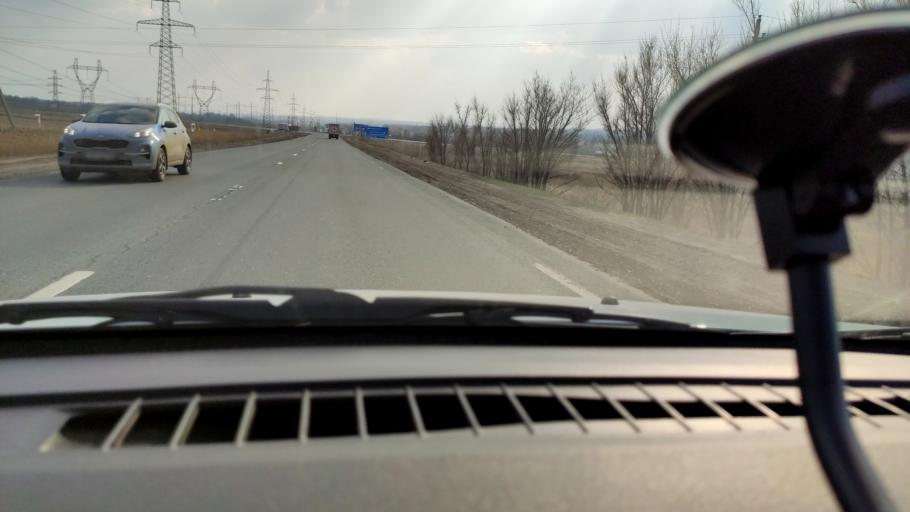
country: RU
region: Samara
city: Dubovyy Umet
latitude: 53.0669
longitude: 50.3782
